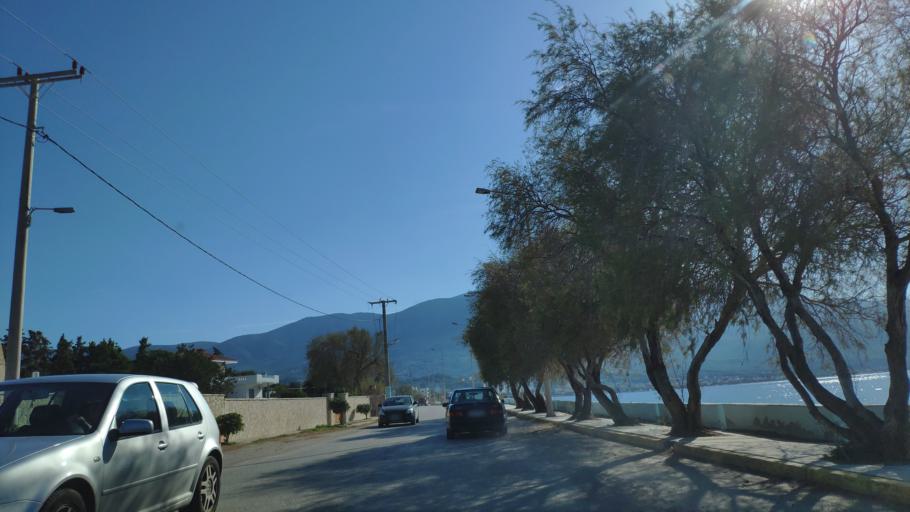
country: GR
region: Attica
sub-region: Nomarchia Dytikis Attikis
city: Kineta
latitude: 38.0854
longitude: 23.1783
